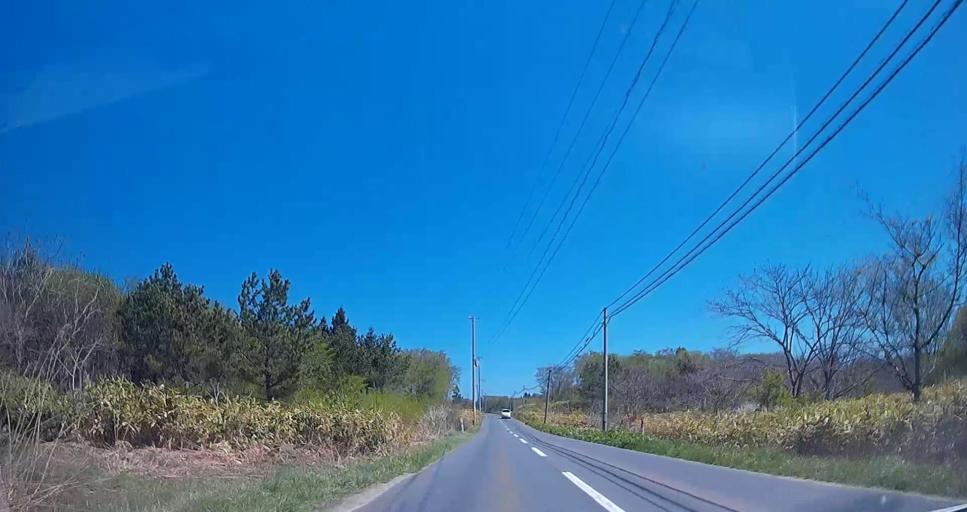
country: JP
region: Aomori
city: Misawa
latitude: 40.9169
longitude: 141.3758
